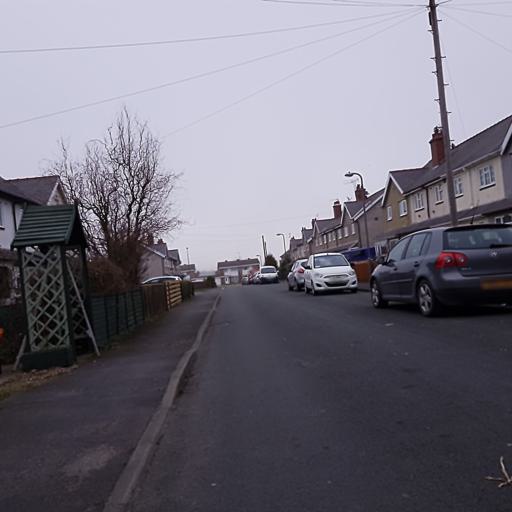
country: GB
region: England
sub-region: North Yorkshire
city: Filey
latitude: 54.2125
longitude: -0.2965
